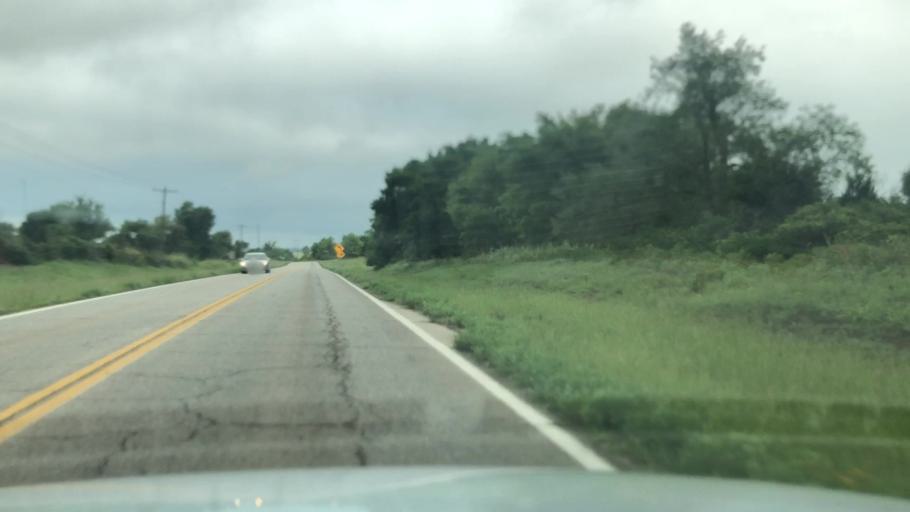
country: US
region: Oklahoma
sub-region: Nowata County
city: Nowata
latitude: 36.7112
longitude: -95.6602
